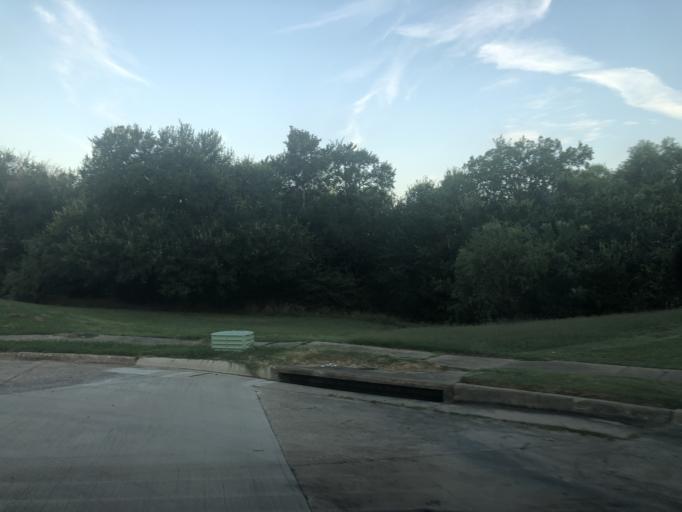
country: US
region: Texas
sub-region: Dallas County
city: Cedar Hill
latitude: 32.6491
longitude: -96.9733
